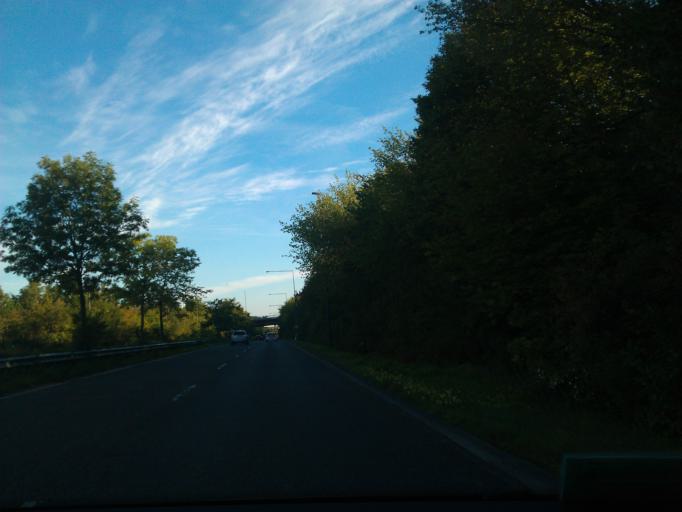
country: DE
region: North Rhine-Westphalia
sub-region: Regierungsbezirk Koln
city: Aachen
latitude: 50.7804
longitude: 6.0518
